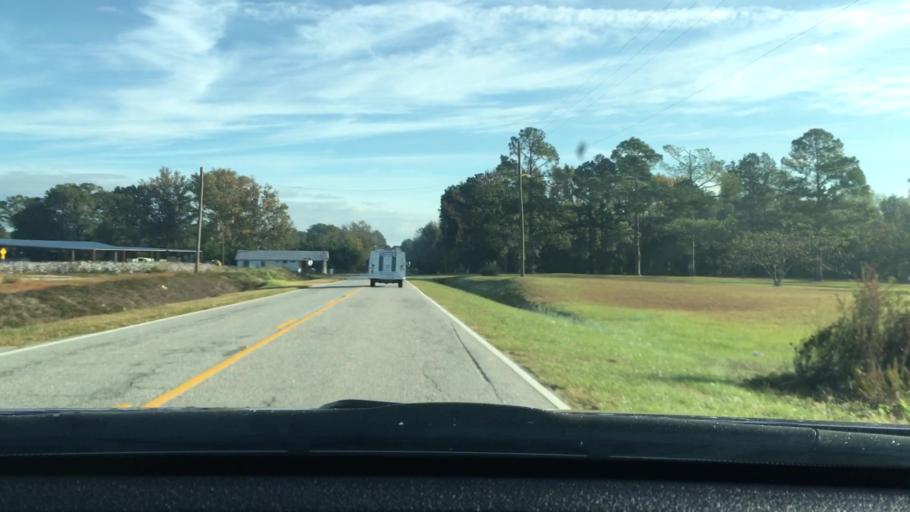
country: US
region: South Carolina
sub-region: Lee County
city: Bishopville
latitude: 34.0737
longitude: -80.2071
